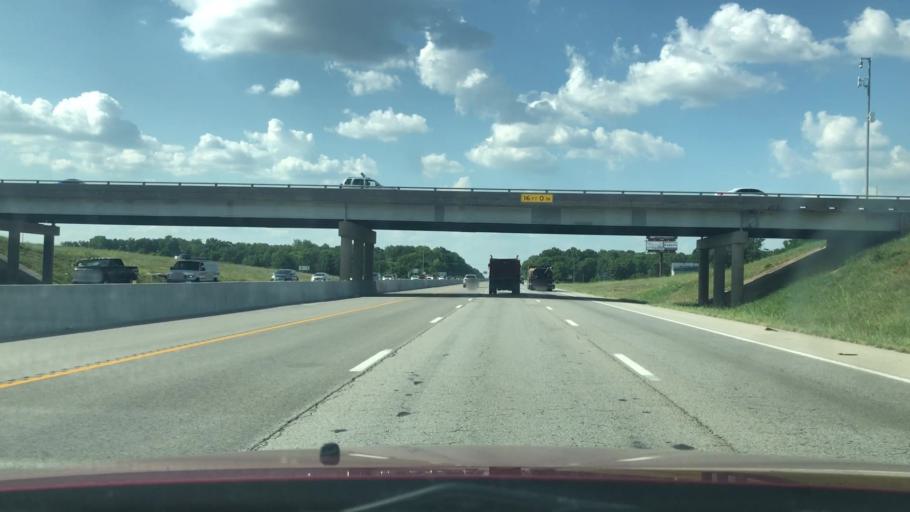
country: US
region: Missouri
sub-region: Christian County
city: Ozark
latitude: 37.1000
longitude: -93.2322
